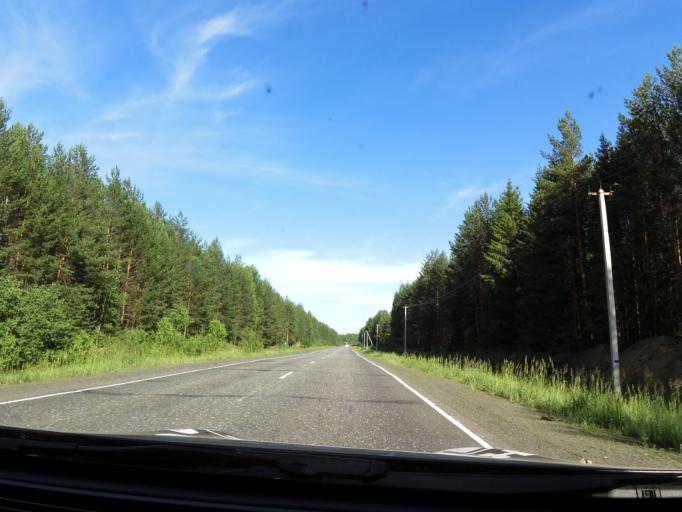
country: RU
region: Kirov
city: Belaya Kholunitsa
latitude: 58.9148
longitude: 51.1556
